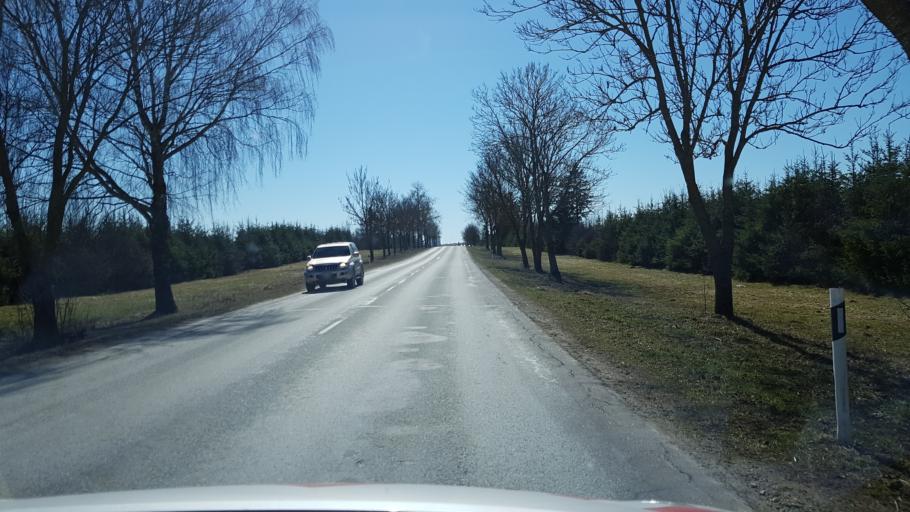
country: EE
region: Laeaene-Virumaa
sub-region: Rakvere linn
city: Rakvere
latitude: 59.3777
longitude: 26.3906
